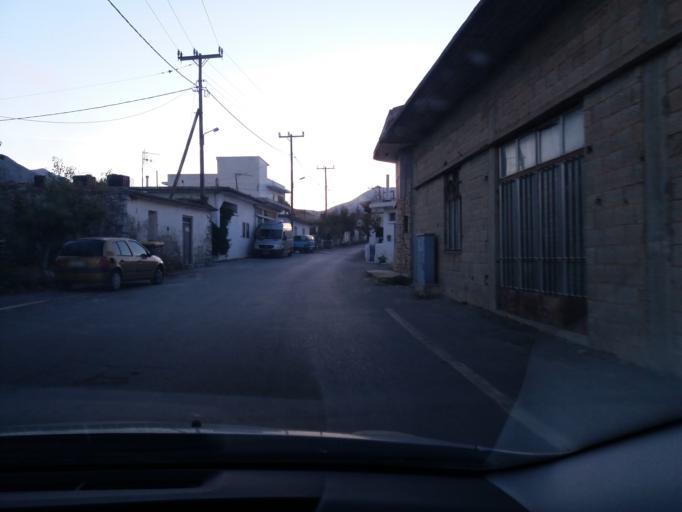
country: GR
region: Crete
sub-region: Nomos Irakleiou
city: Mokhos
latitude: 35.1671
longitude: 25.4869
